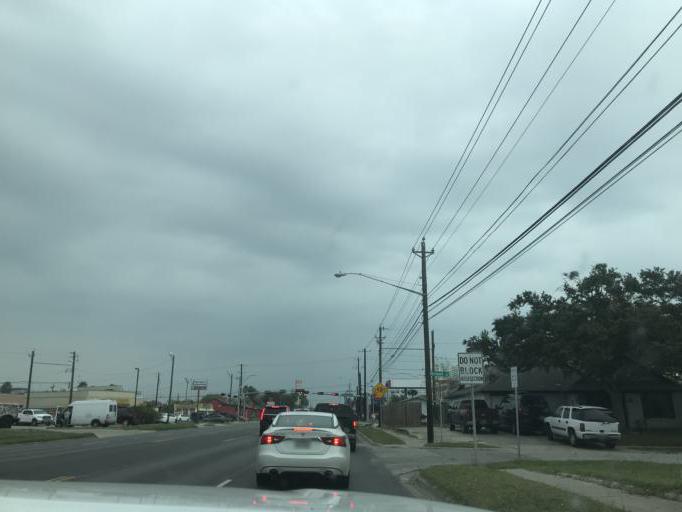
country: US
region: Texas
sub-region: Nueces County
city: Corpus Christi
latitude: 27.6989
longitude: -97.3630
